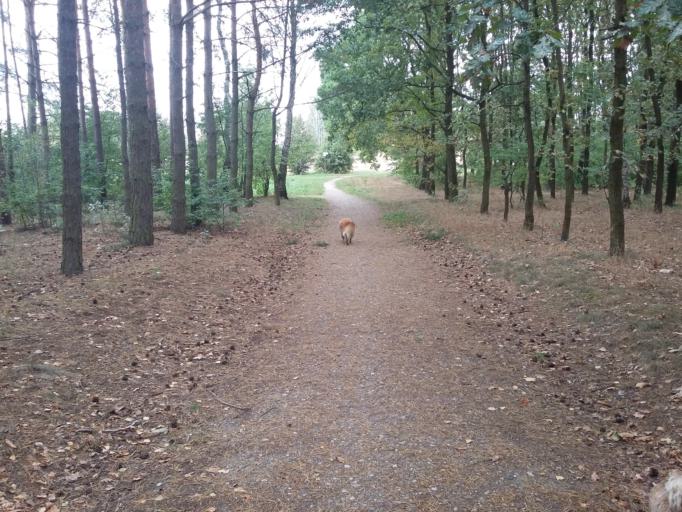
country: PL
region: Lodz Voivodeship
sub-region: Powiat pabianicki
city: Ksawerow
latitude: 51.7281
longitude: 19.3870
